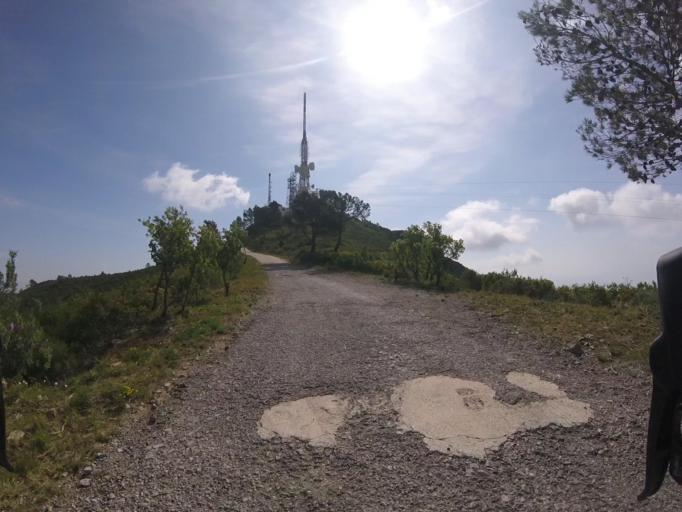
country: ES
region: Valencia
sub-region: Provincia de Castello
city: Benicassim
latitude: 40.0857
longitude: 0.0294
